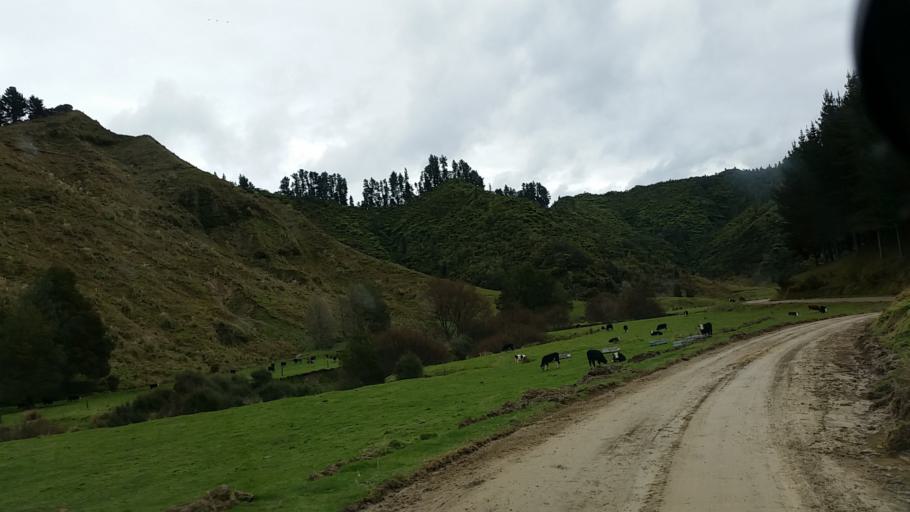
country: NZ
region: Taranaki
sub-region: South Taranaki District
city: Patea
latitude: -39.6679
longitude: 174.7488
